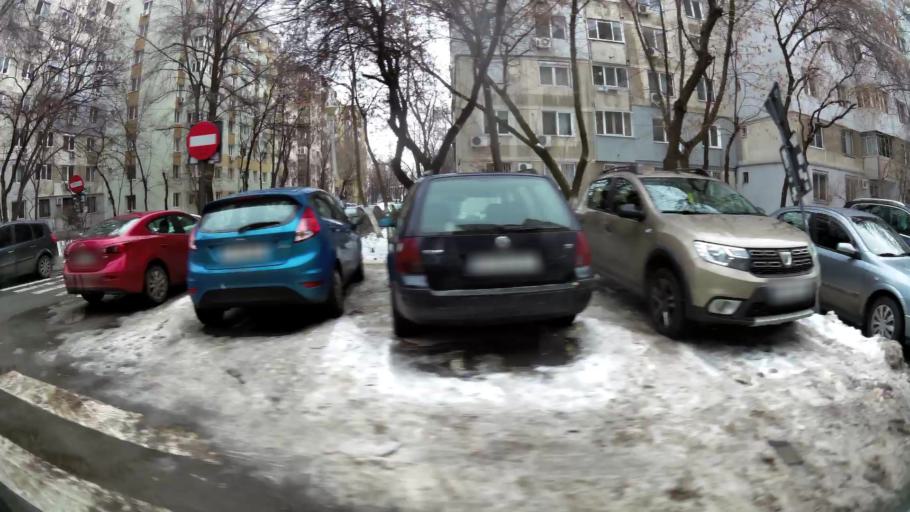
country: RO
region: Ilfov
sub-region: Comuna Chiajna
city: Rosu
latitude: 44.4168
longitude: 26.0469
